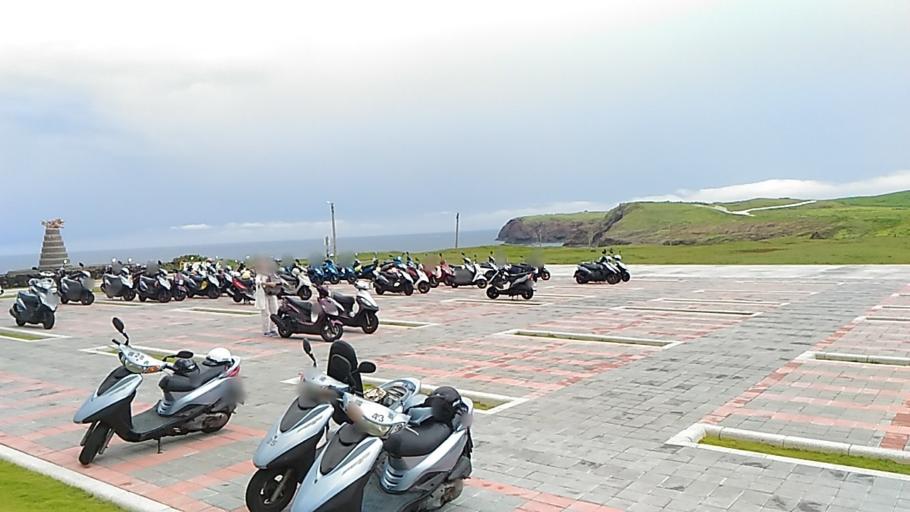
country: TW
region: Taiwan
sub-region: Penghu
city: Ma-kung
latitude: 23.2191
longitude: 119.4462
